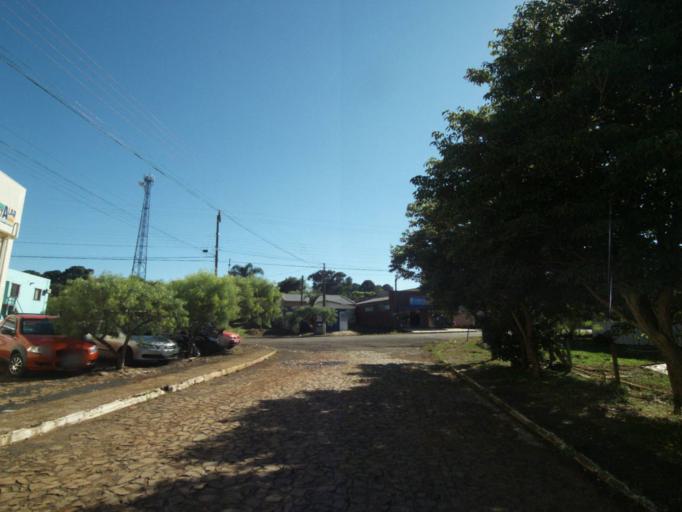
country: BR
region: Parana
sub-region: Pinhao
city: Pinhao
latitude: -25.8355
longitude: -52.0272
